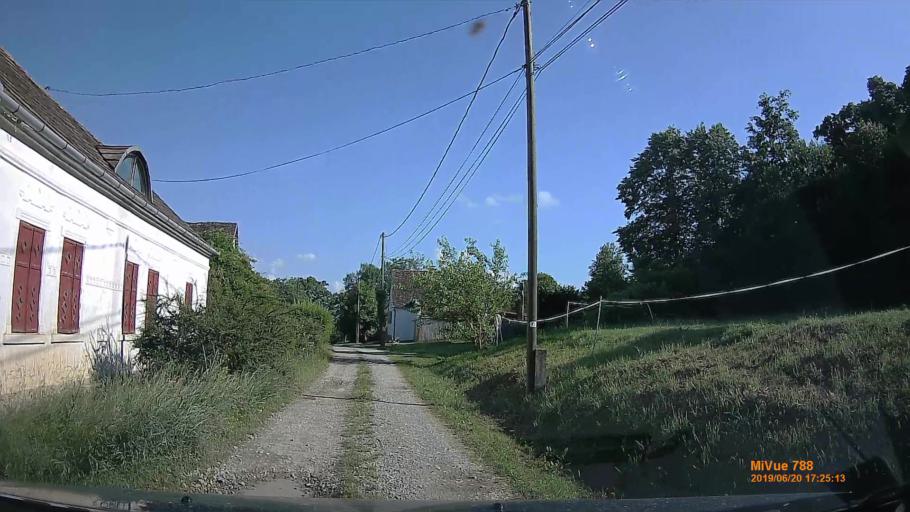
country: HU
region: Baranya
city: Buekkoesd
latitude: 46.1633
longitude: 18.0092
